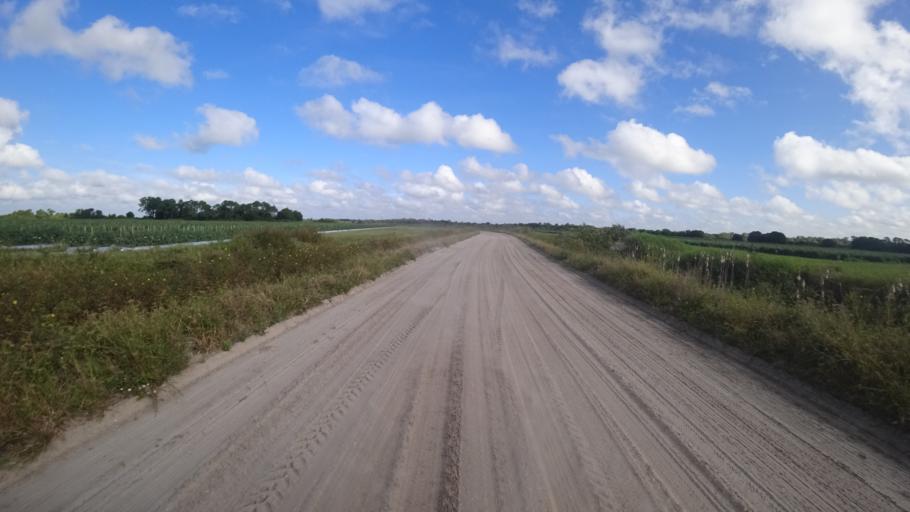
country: US
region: Florida
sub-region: Hillsborough County
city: Wimauma
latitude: 27.5496
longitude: -82.3209
